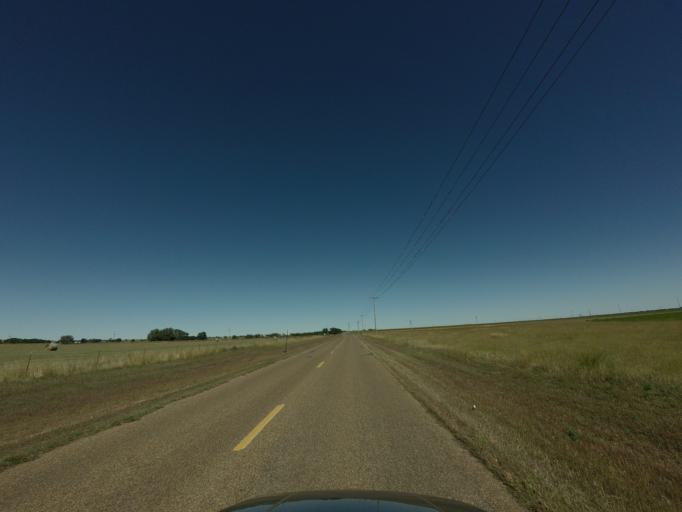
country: US
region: New Mexico
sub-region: Curry County
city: Clovis
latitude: 34.4314
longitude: -103.1608
